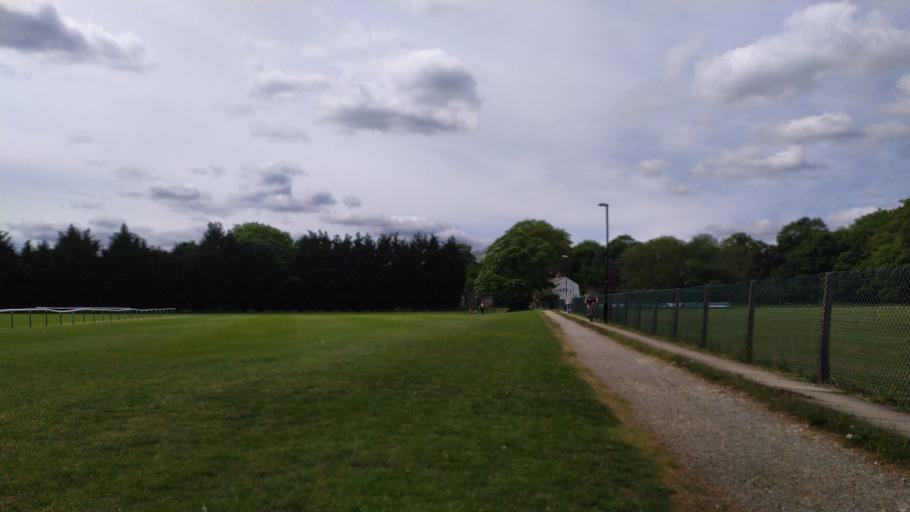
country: GB
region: England
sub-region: City and Borough of Leeds
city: Horsforth
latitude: 53.8359
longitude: -1.5900
